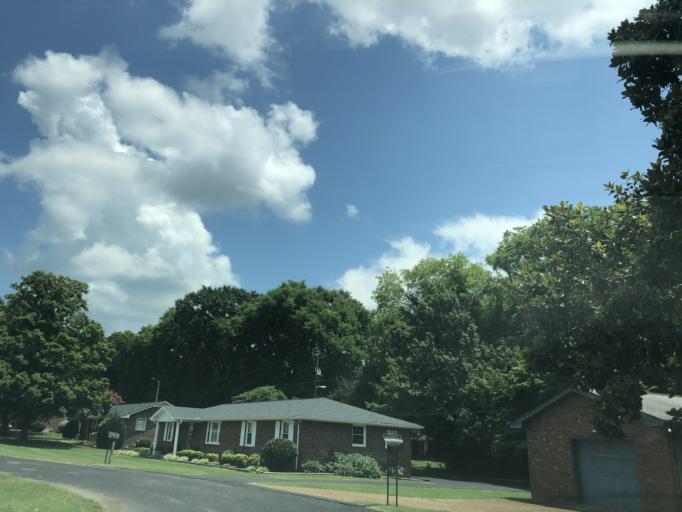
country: US
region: Tennessee
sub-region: Davidson County
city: Lakewood
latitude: 36.2050
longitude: -86.6099
